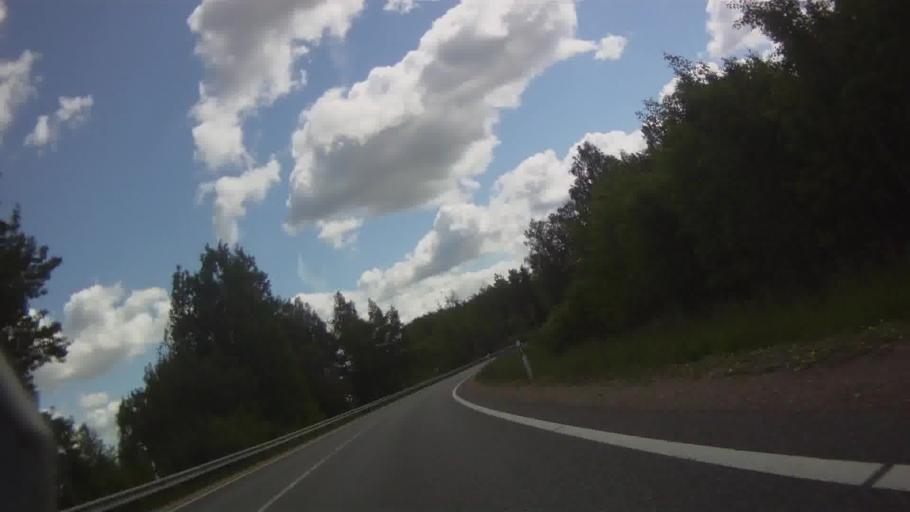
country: LV
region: Livani
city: Livani
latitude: 56.5459
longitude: 26.1176
